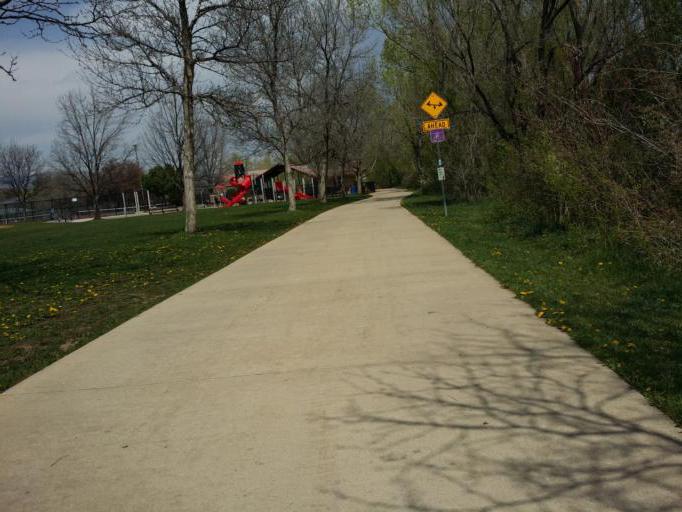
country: US
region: Colorado
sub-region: Boulder County
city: Boulder
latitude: 39.9875
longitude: -105.2499
